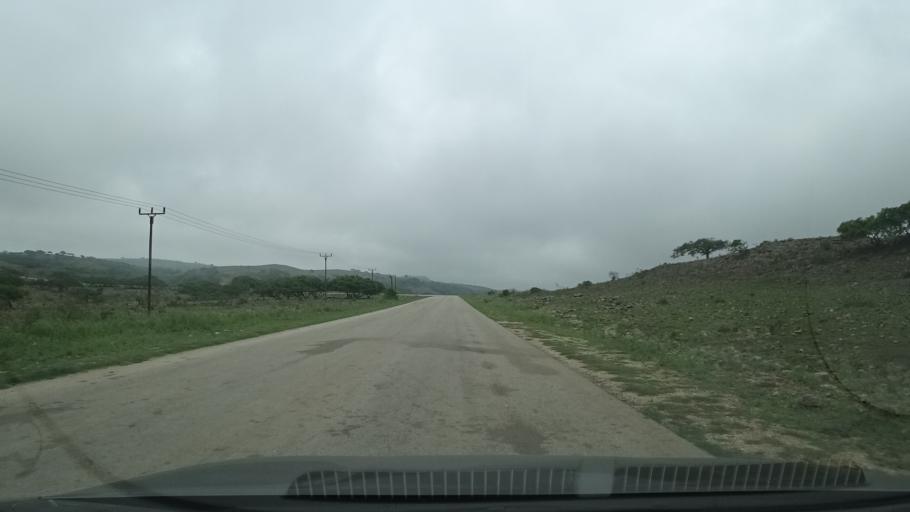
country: OM
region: Zufar
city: Salalah
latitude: 17.1180
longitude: 54.5715
